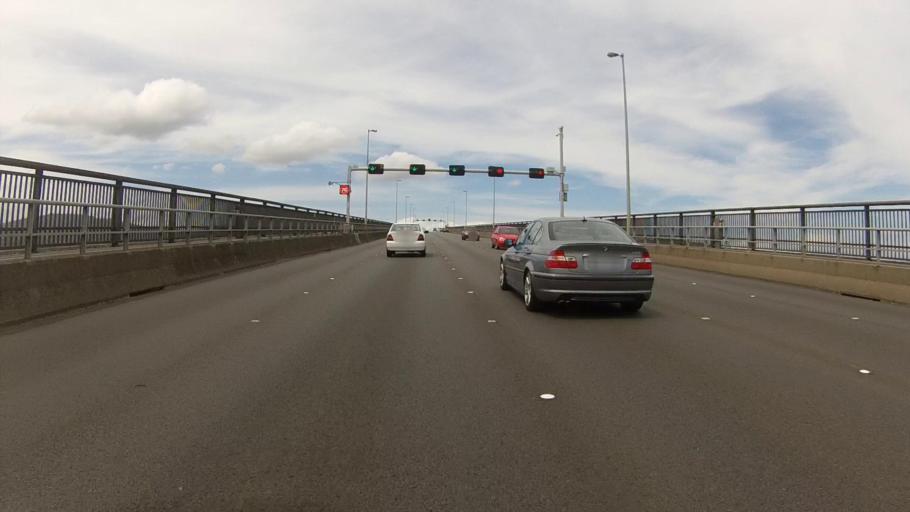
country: AU
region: Tasmania
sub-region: Hobart
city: Hobart
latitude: -42.8651
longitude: 147.3385
